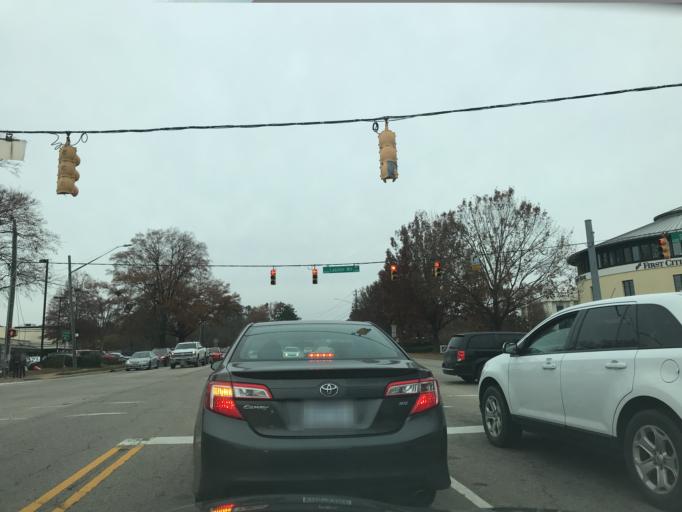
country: US
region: North Carolina
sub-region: Wake County
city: West Raleigh
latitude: 35.8393
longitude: -78.6422
